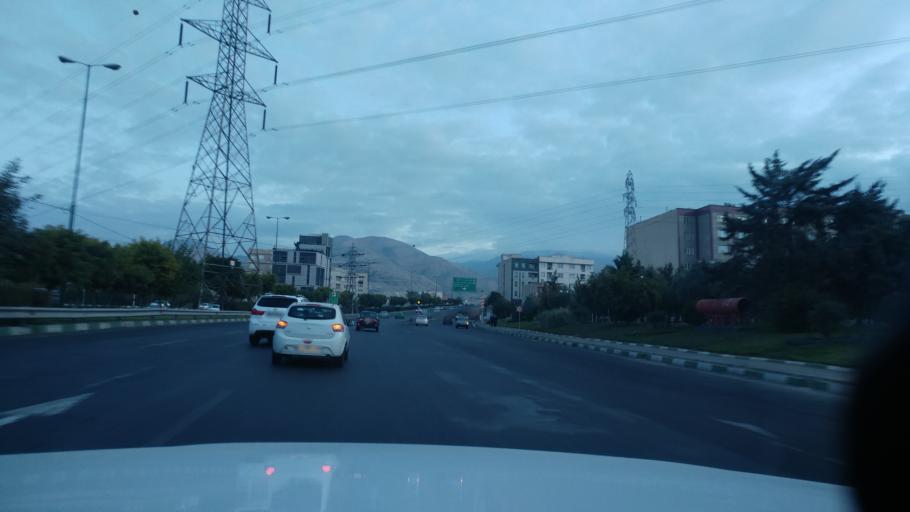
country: IR
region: Tehran
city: Tehran
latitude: 35.7471
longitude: 51.3146
